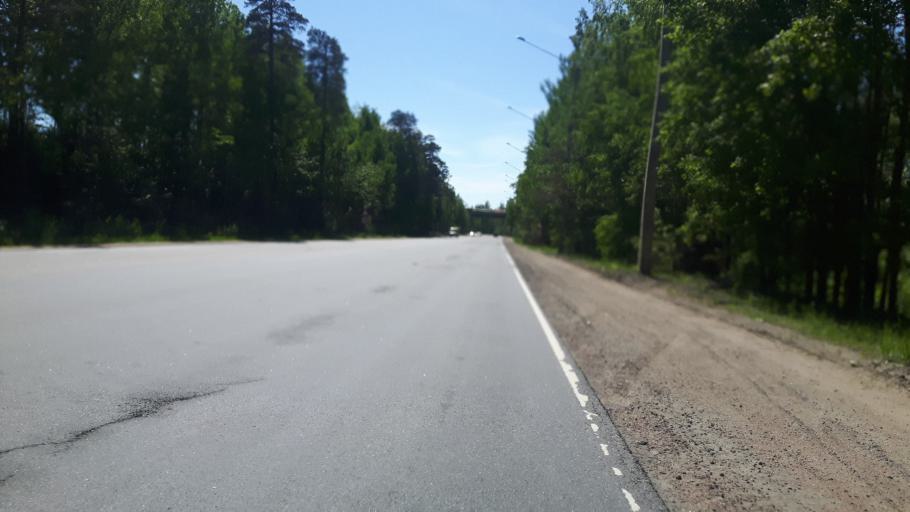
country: RU
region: Leningrad
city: Sosnovyy Bor
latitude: 59.8663
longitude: 29.0724
